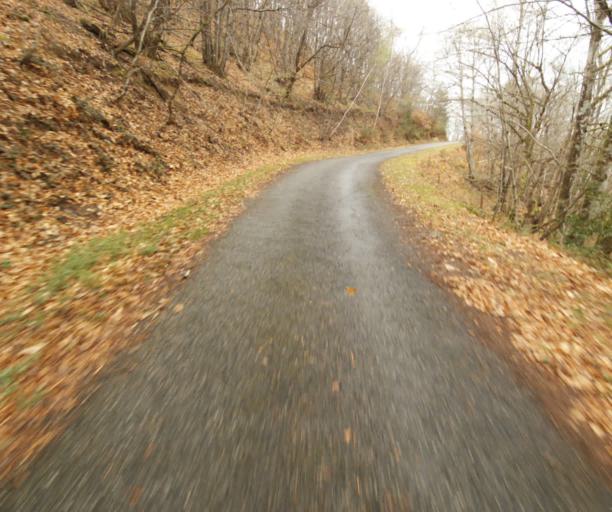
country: FR
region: Limousin
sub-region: Departement de la Correze
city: Saint-Privat
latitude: 45.2160
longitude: 2.0323
